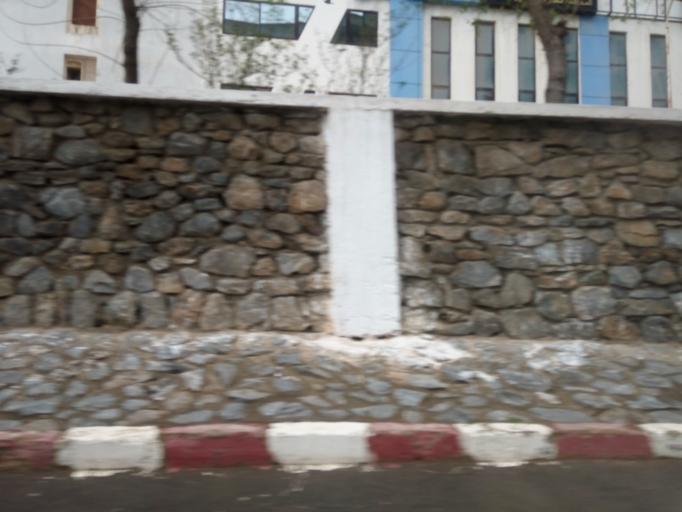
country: DZ
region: Tipaza
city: Saoula
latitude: 36.7343
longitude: 2.9935
